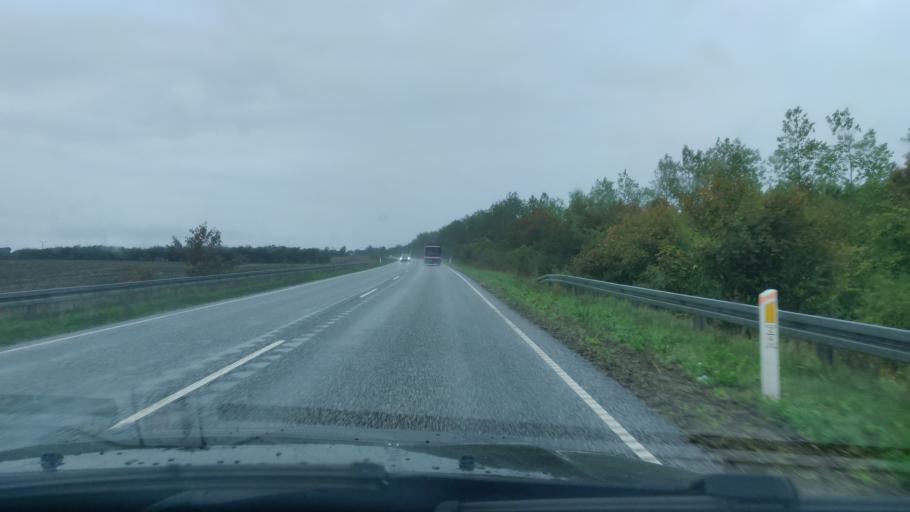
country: DK
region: North Denmark
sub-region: Thisted Kommune
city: Thisted
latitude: 56.9704
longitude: 8.7198
